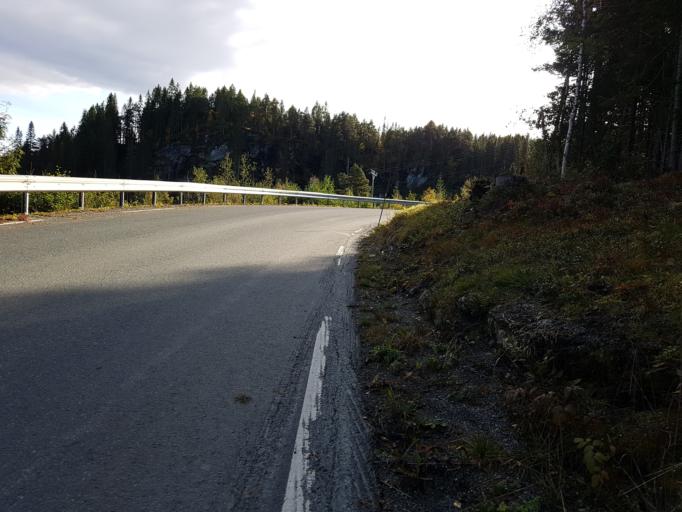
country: NO
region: Sor-Trondelag
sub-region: Klaebu
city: Klaebu
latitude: 63.3474
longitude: 10.5367
